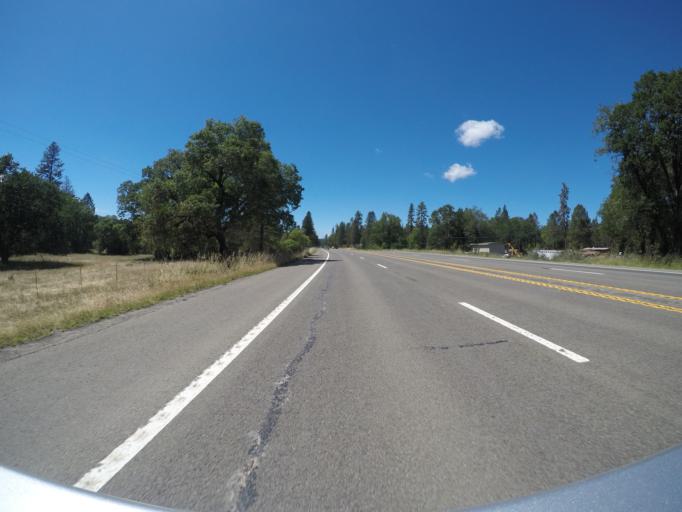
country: US
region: California
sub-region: Mendocino County
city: Laytonville
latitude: 39.7287
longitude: -123.5061
